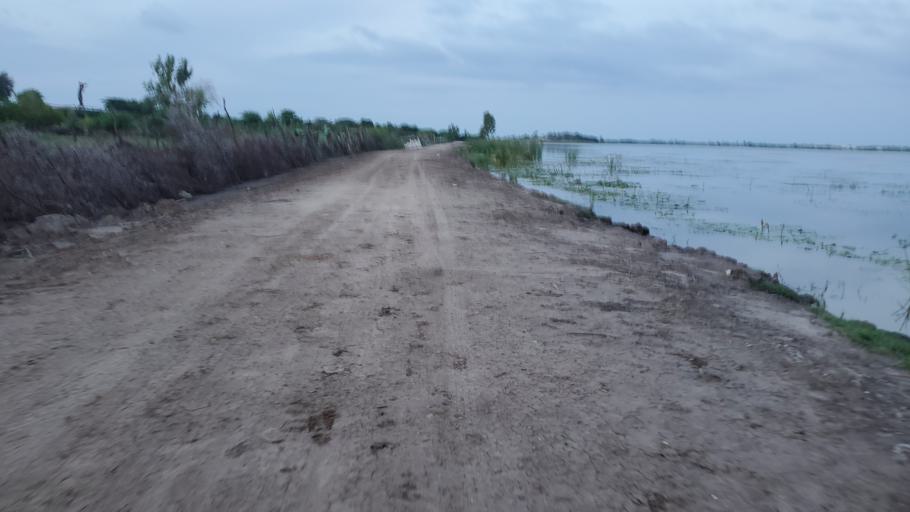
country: SN
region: Saint-Louis
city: Saint-Louis
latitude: 16.0478
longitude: -16.4147
